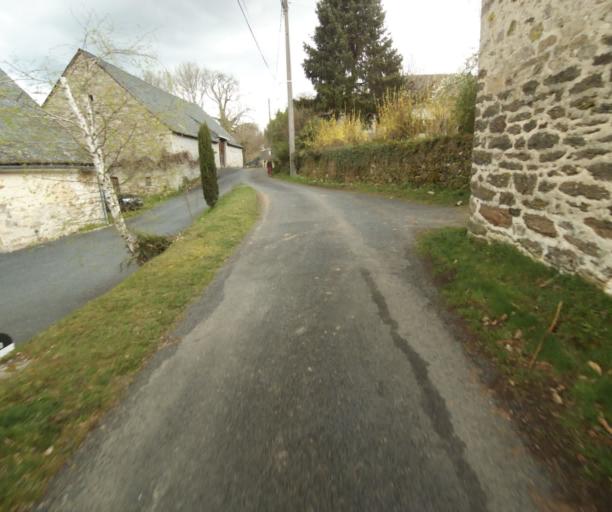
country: FR
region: Limousin
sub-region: Departement de la Correze
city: Laguenne
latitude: 45.2438
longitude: 1.8881
